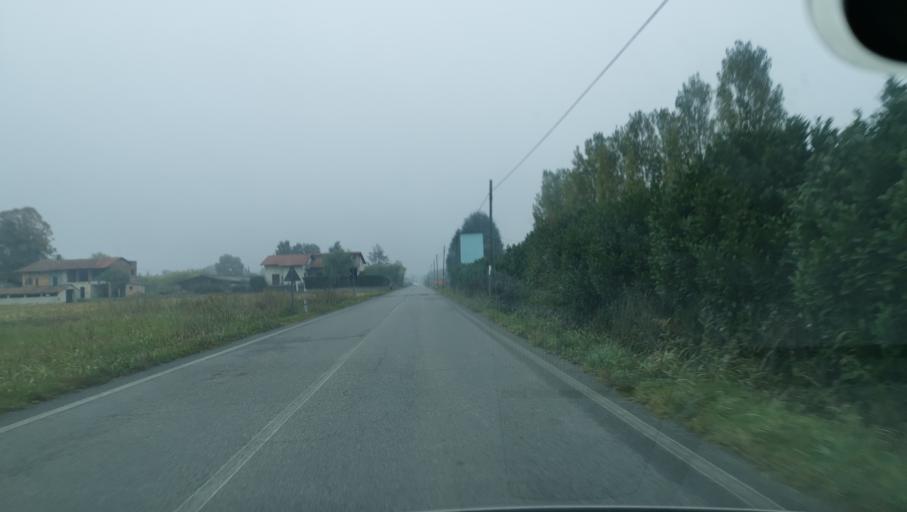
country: IT
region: Piedmont
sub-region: Provincia di Biella
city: Cavaglia
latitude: 45.3887
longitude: 8.0867
